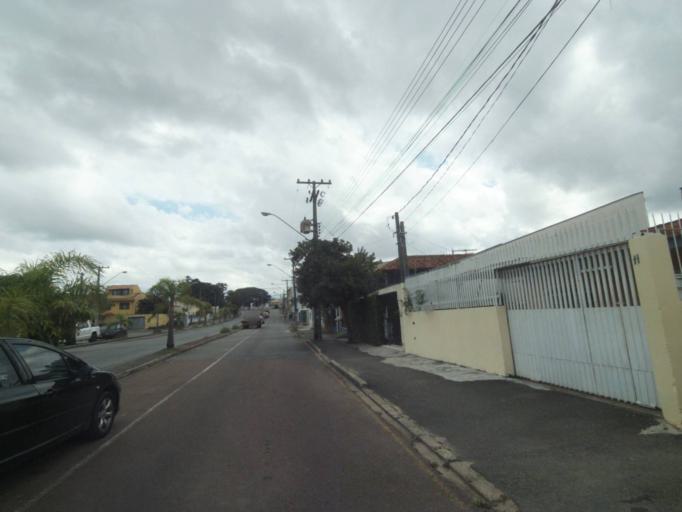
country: BR
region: Parana
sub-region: Pinhais
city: Pinhais
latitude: -25.4451
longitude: -49.2164
